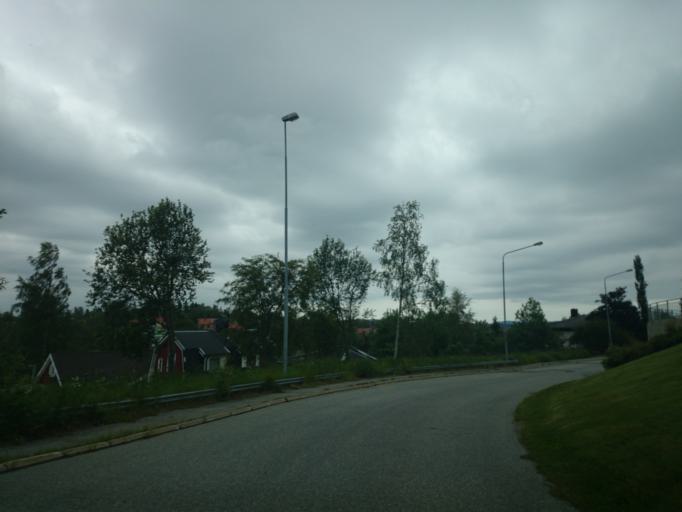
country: SE
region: Vaesternorrland
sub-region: Haernoesands Kommun
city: Haernoesand
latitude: 62.6300
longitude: 17.9206
